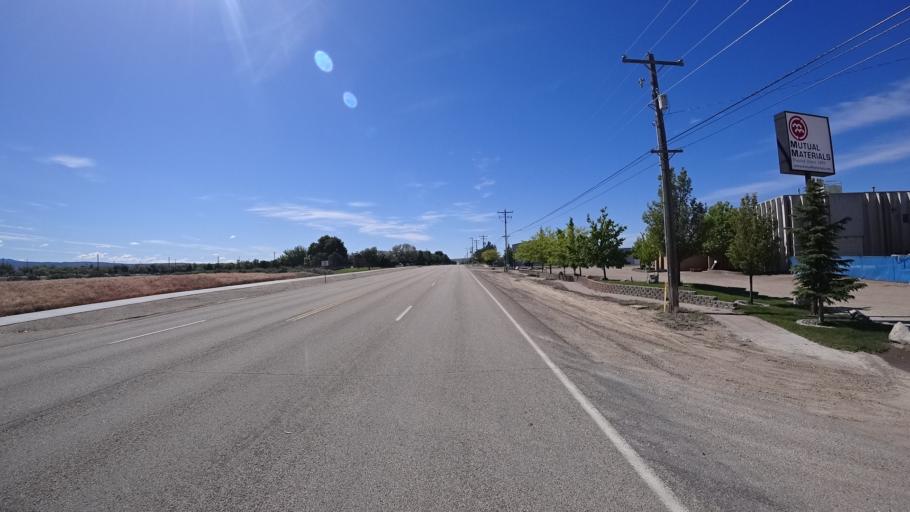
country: US
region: Idaho
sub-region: Ada County
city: Boise
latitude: 43.5350
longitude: -116.1532
